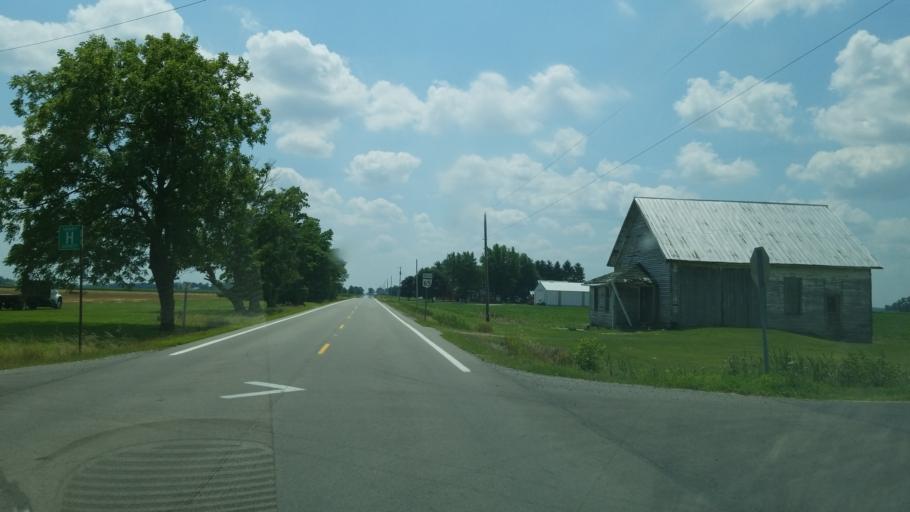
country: US
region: Ohio
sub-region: Henry County
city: Deshler
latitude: 41.2694
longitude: -83.9405
